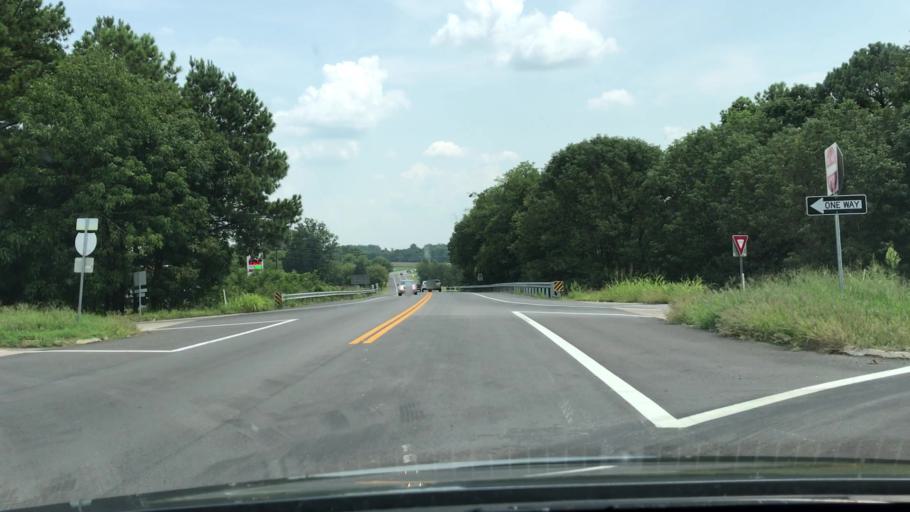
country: US
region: Tennessee
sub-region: Sumner County
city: Portland
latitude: 36.5909
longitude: -86.5989
